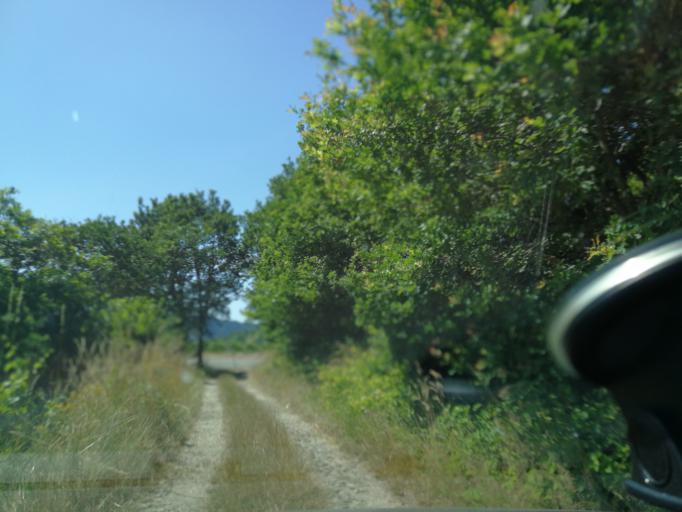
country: DE
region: Rheinland-Pfalz
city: Wintrich
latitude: 49.8840
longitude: 6.9406
